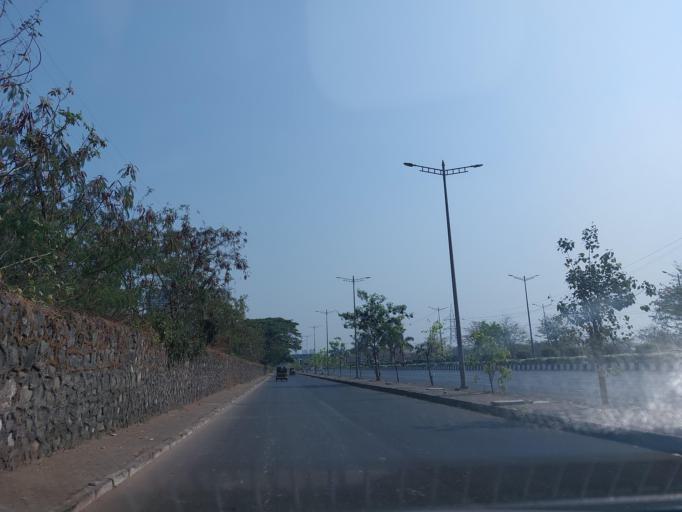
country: IN
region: Maharashtra
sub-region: Mumbai Suburban
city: Powai
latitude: 19.0971
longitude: 72.9272
